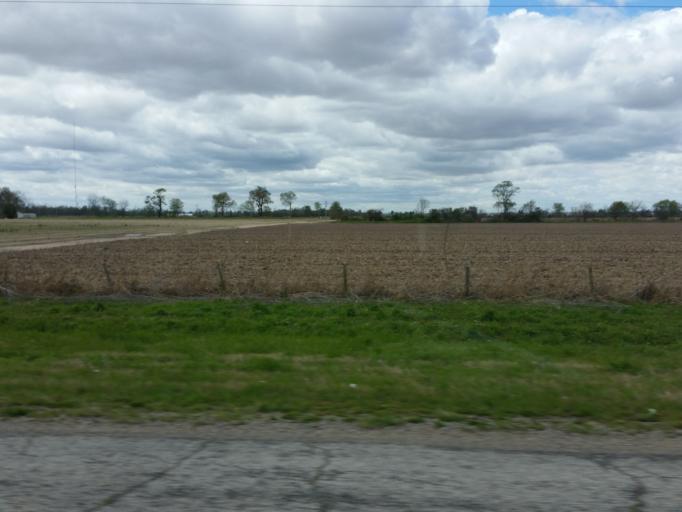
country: US
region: Arkansas
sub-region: Poinsett County
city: Trumann
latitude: 35.6130
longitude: -90.4968
